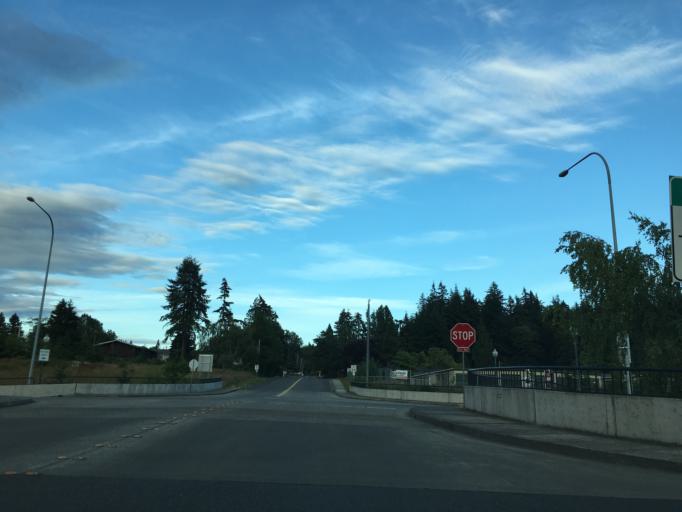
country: US
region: Washington
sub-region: Whatcom County
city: Blaine
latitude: 48.9981
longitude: -122.7355
